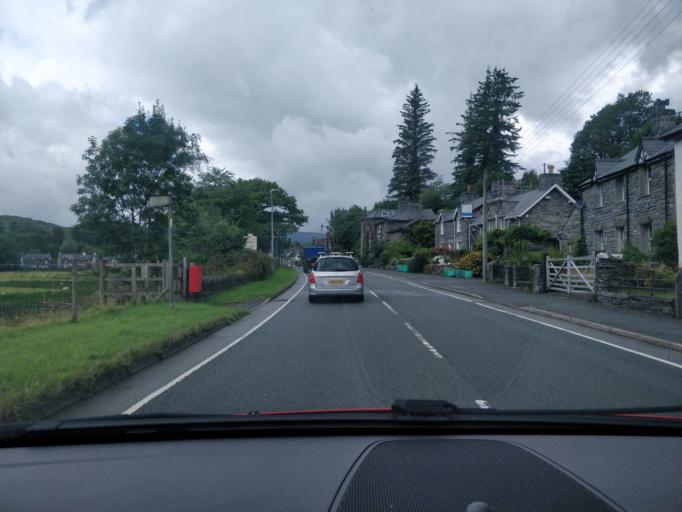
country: GB
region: Wales
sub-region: Gwynedd
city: Blaenau-Ffestiniog
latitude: 53.0548
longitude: -3.8845
